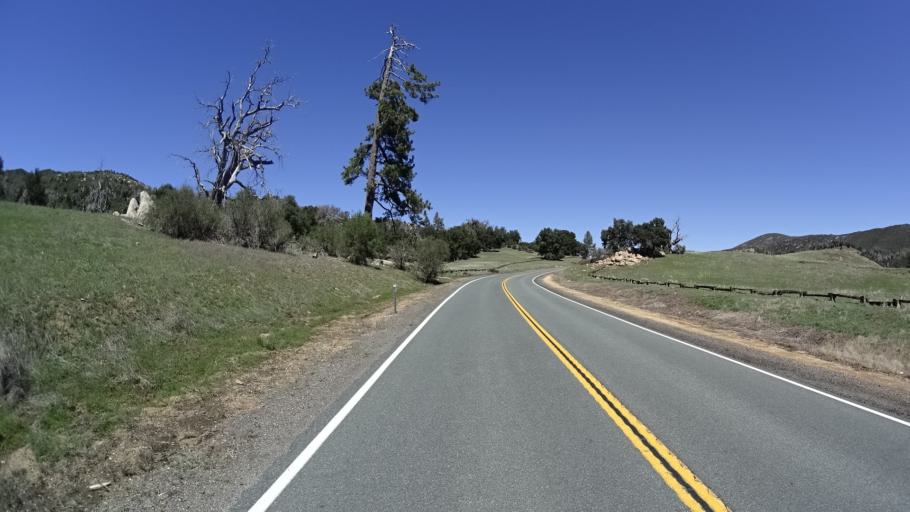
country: US
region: California
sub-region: San Diego County
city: Descanso
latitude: 32.9131
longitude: -116.5737
